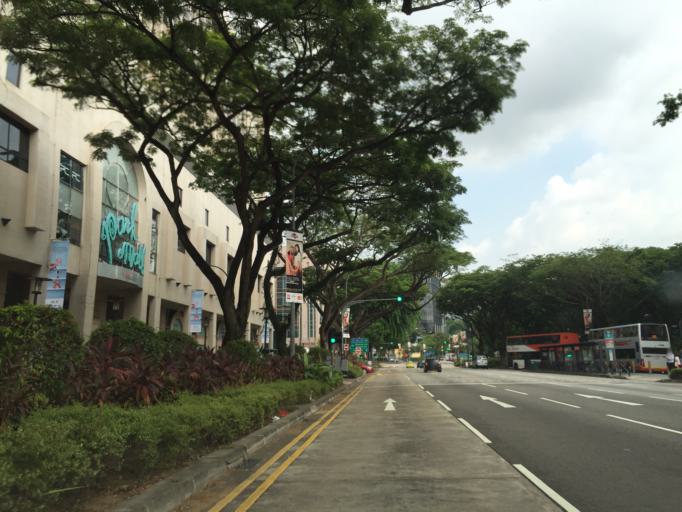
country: SG
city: Singapore
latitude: 1.2981
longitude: 103.8456
